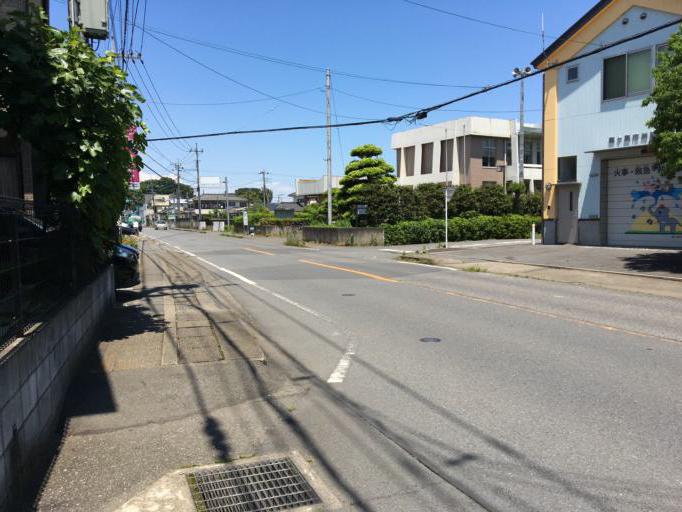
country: JP
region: Saitama
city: Sakado
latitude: 35.9384
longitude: 139.3884
